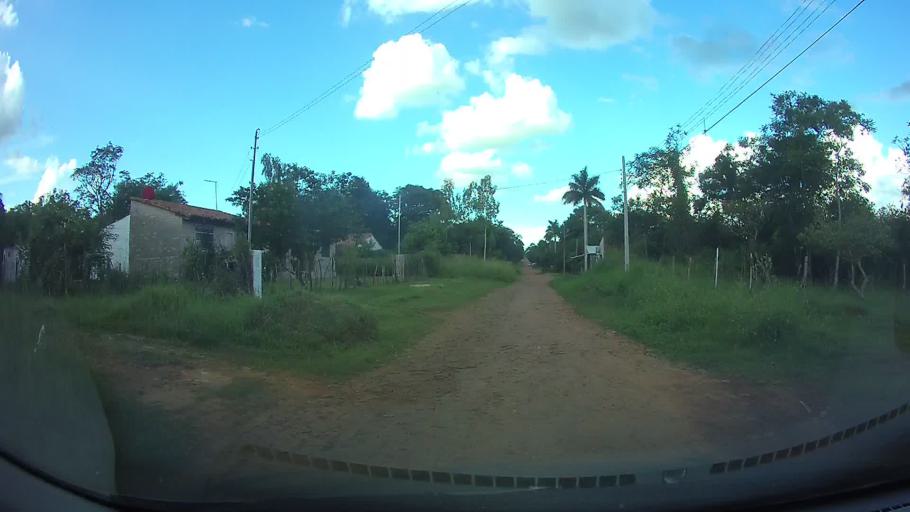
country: PY
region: Central
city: Limpio
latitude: -25.2523
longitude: -57.4592
